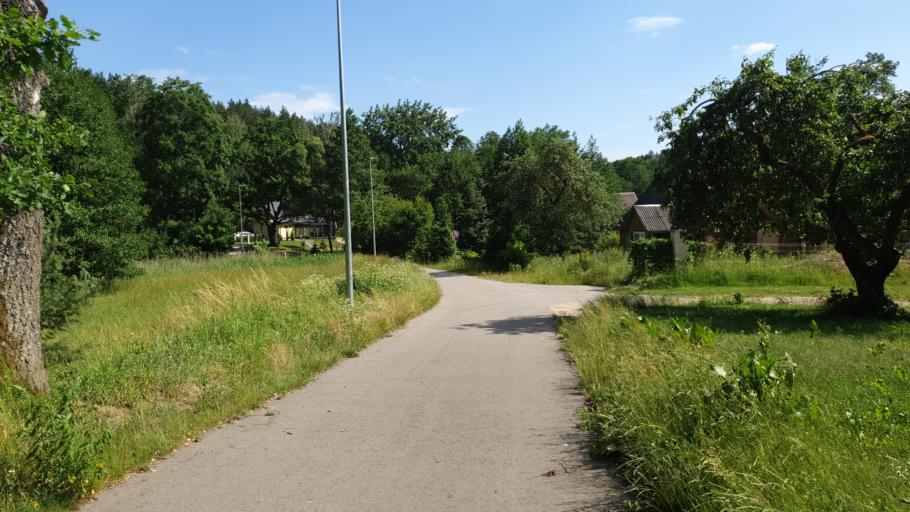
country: LT
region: Vilnius County
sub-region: Vilnius
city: Fabijoniskes
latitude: 54.7845
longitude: 25.3260
